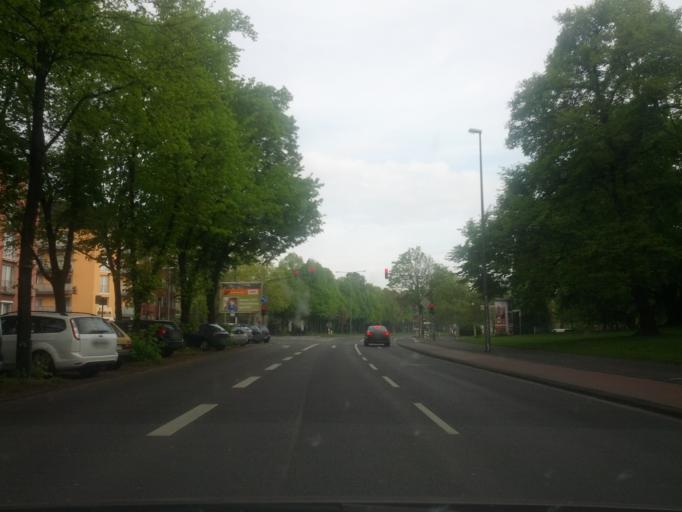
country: DE
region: North Rhine-Westphalia
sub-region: Regierungsbezirk Koln
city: Neustadt/Sued
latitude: 50.9329
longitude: 6.9252
